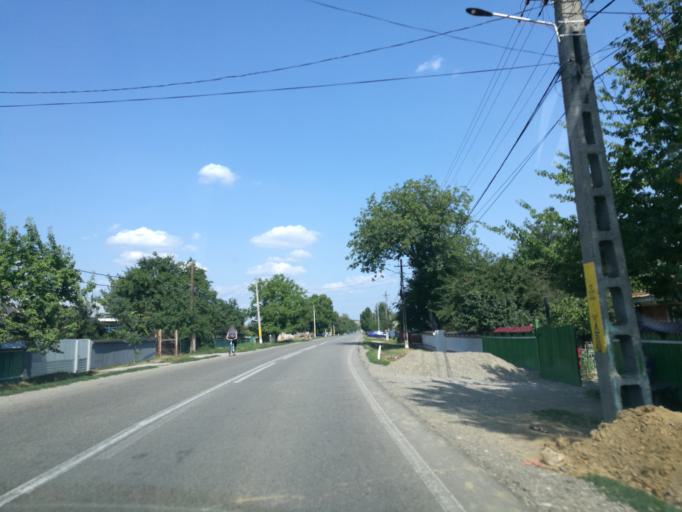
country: RO
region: Neamt
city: Bodesti
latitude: 47.0384
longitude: 26.4089
